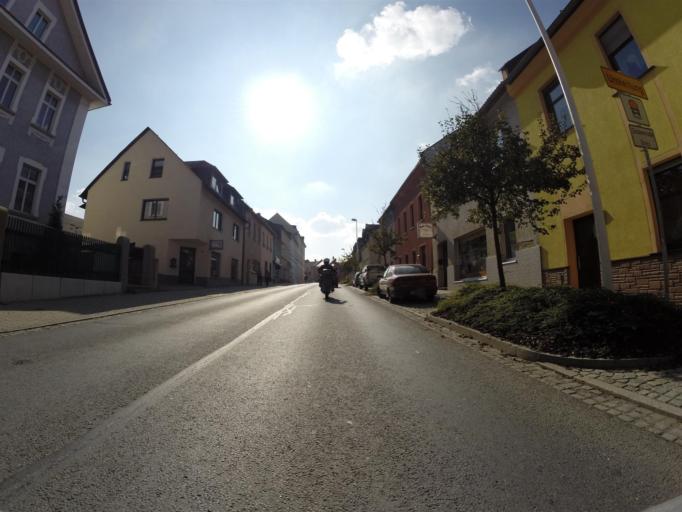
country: DE
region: Thuringia
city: Schleiz
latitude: 50.5792
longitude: 11.8079
